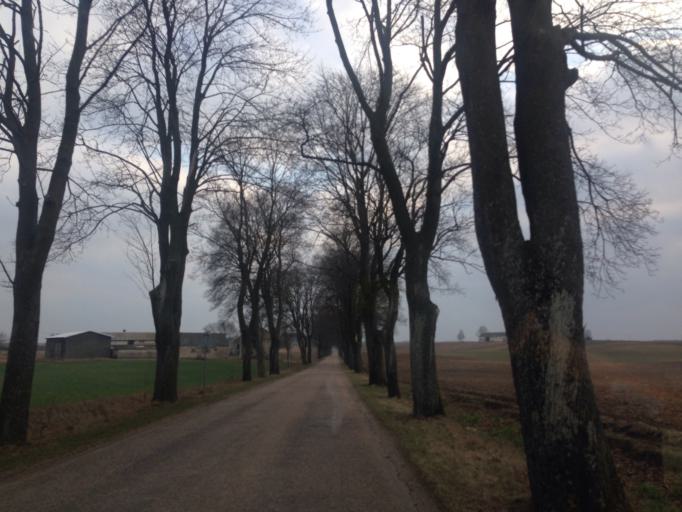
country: PL
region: Kujawsko-Pomorskie
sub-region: Powiat brodnicki
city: Brzozie
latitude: 53.3424
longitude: 19.7132
